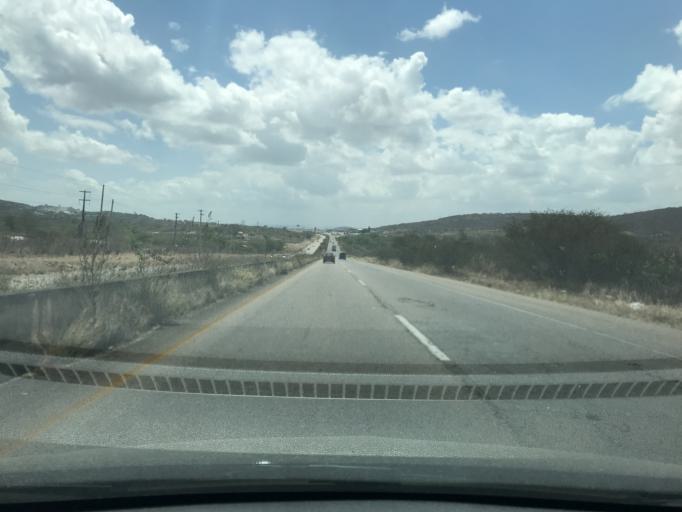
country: BR
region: Pernambuco
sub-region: Bezerros
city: Bezerros
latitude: -8.2962
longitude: -35.8708
